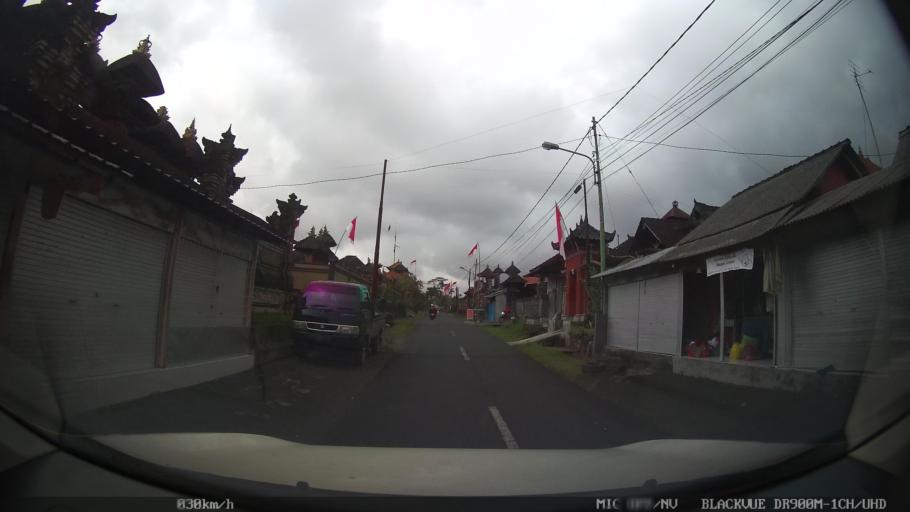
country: ID
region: Bali
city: Banjar Sempidi
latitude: -8.5239
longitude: 115.1905
